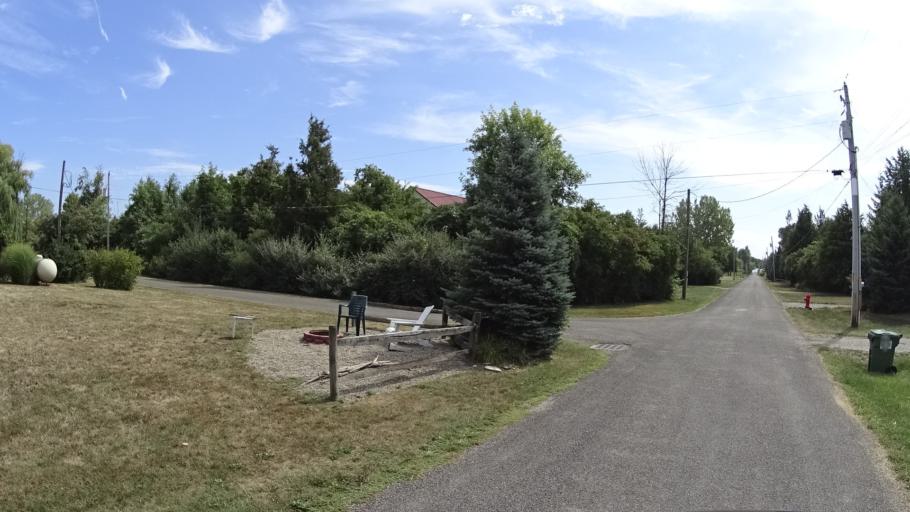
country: US
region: Ohio
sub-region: Erie County
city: Sandusky
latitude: 41.5920
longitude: -82.6944
